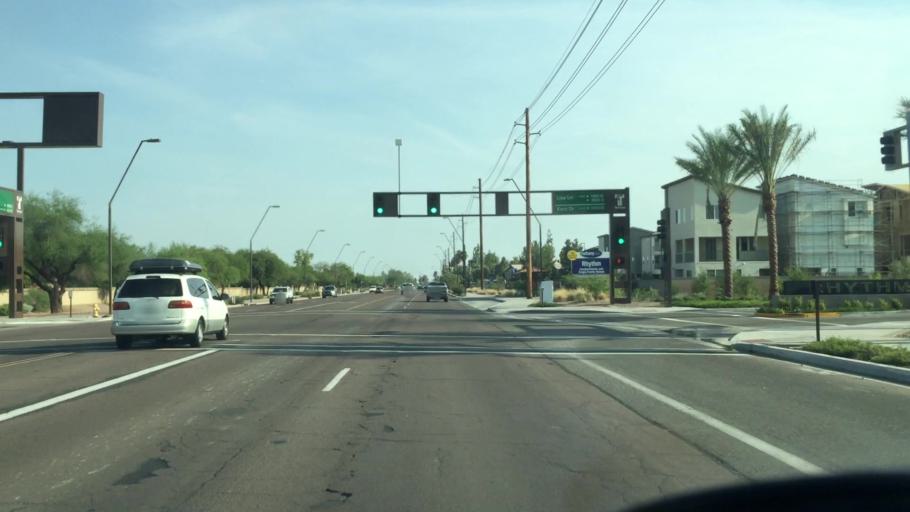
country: US
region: Arizona
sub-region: Maricopa County
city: Guadalupe
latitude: 33.3262
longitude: -111.9632
